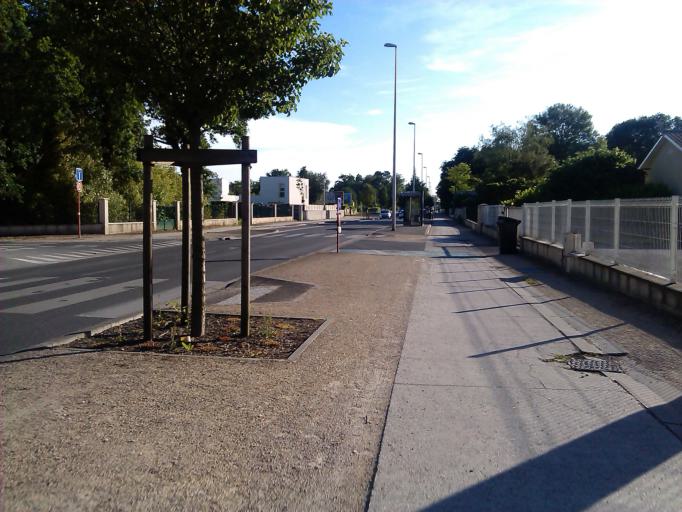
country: FR
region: Aquitaine
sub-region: Departement de la Gironde
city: Cestas
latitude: 44.7854
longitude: -0.6826
